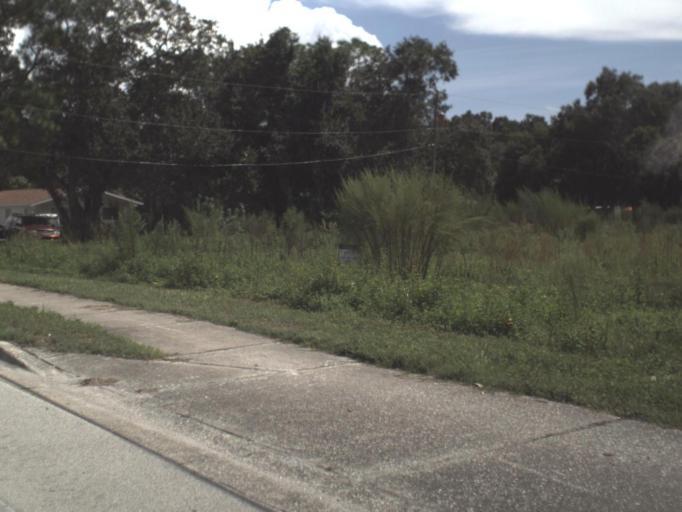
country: US
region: Florida
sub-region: Manatee County
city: Samoset
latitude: 27.4472
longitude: -82.5182
